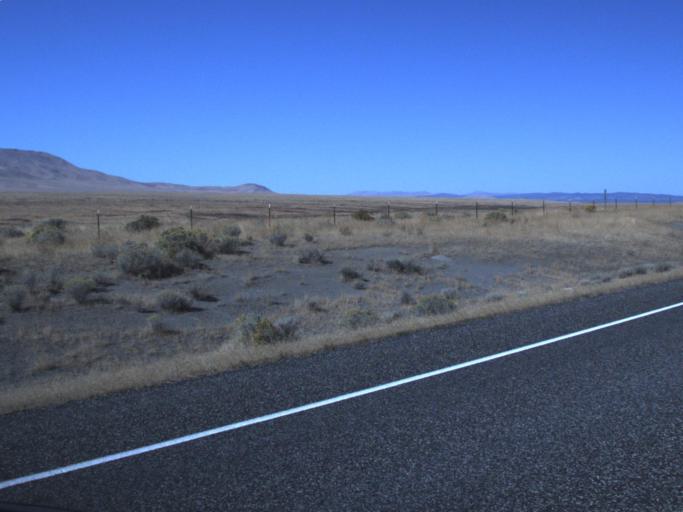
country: US
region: Washington
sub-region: Benton County
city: West Richland
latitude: 46.4080
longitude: -119.4501
